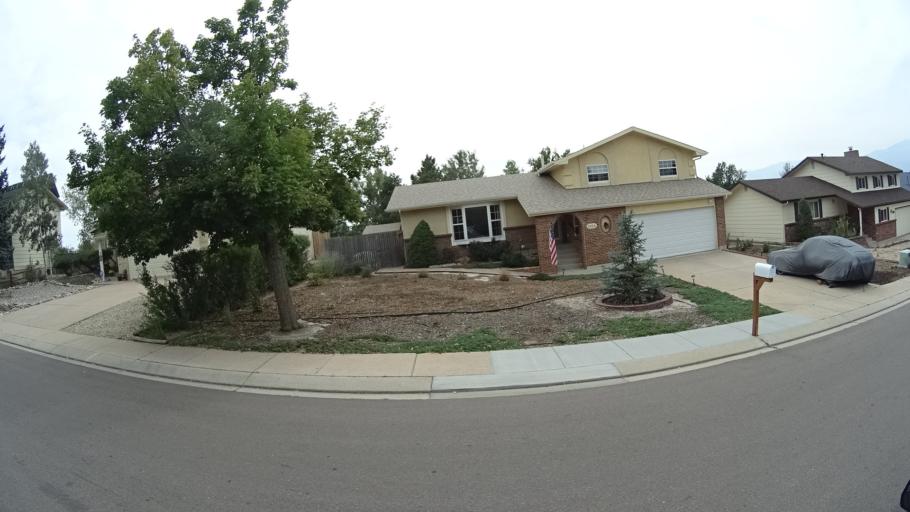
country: US
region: Colorado
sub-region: El Paso County
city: Cimarron Hills
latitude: 38.8895
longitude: -104.7311
